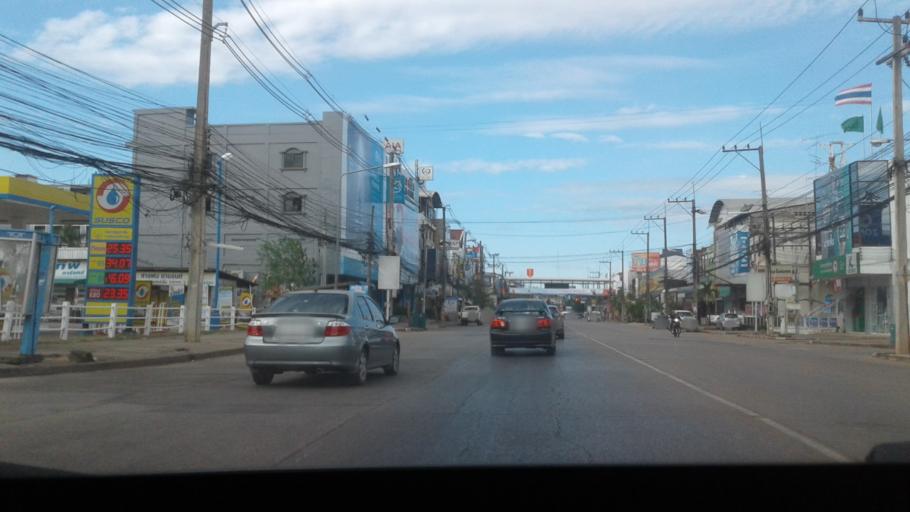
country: TH
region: Changwat Udon Thani
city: Udon Thani
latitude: 17.4213
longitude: 102.7909
